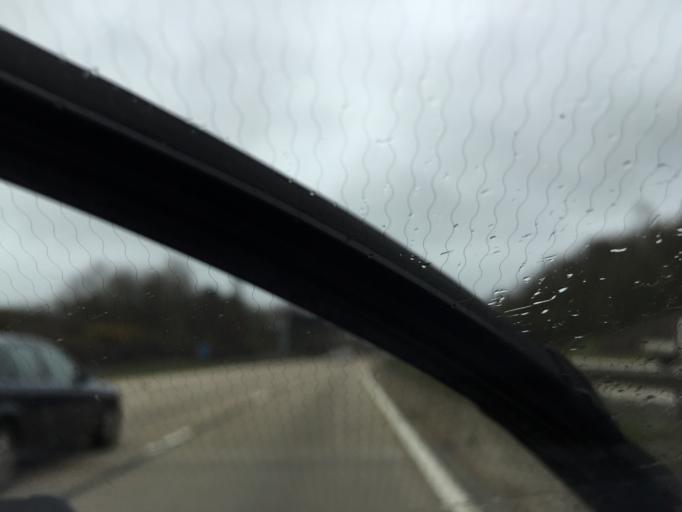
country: GB
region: England
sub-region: Hampshire
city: West End
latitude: 50.9353
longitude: -1.3334
